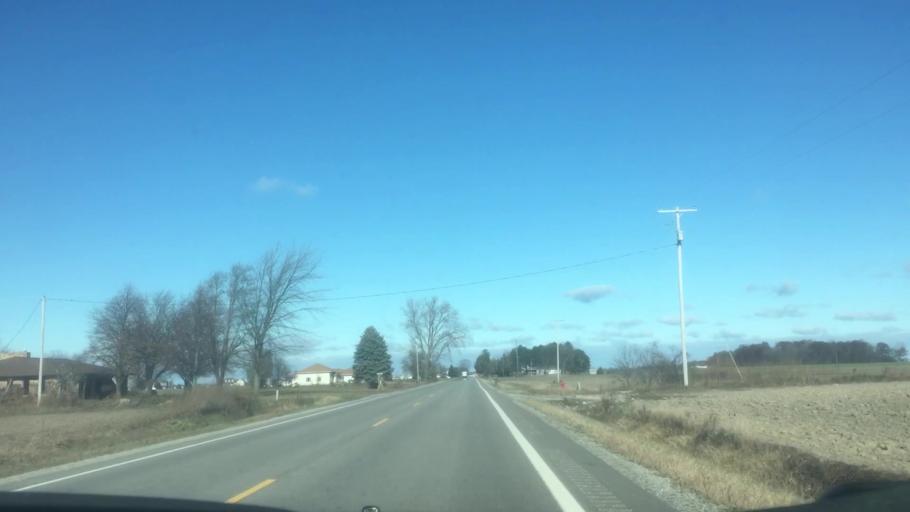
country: US
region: Michigan
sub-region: Bay County
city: Essexville
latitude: 43.5433
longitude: -83.7589
